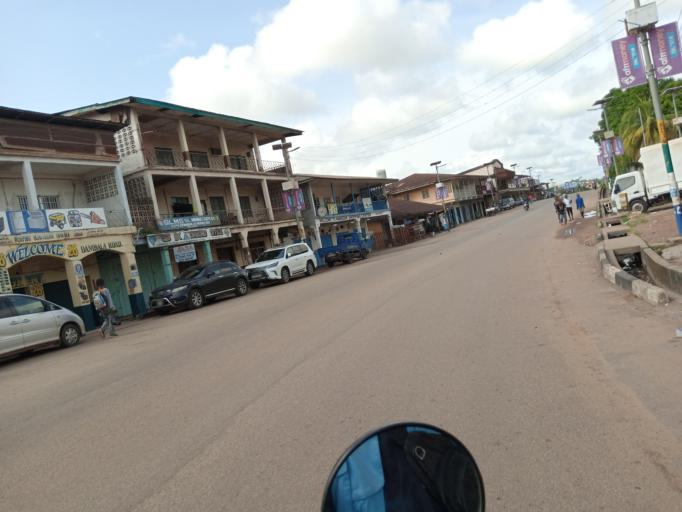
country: SL
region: Southern Province
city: Bo
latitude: 7.9639
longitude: -11.7396
